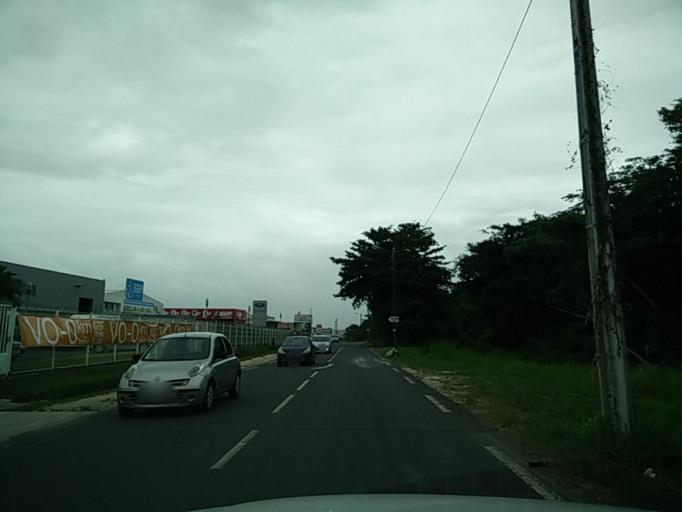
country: GP
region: Guadeloupe
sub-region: Guadeloupe
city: Baie-Mahault
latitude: 16.2531
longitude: -61.5695
